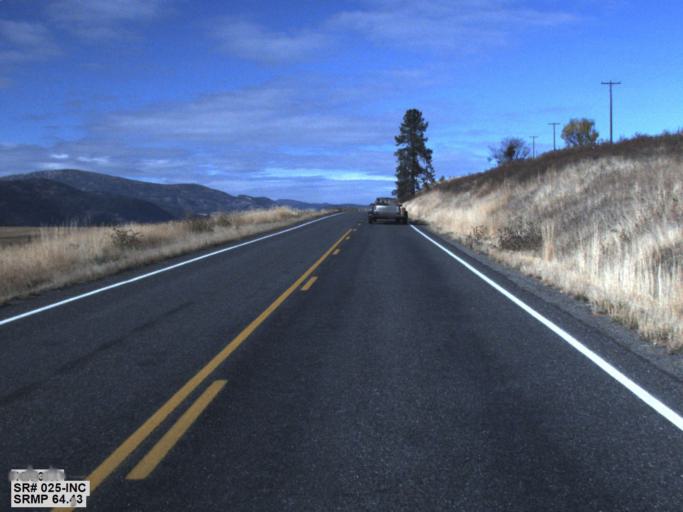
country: US
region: Washington
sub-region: Stevens County
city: Kettle Falls
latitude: 48.4017
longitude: -118.1689
